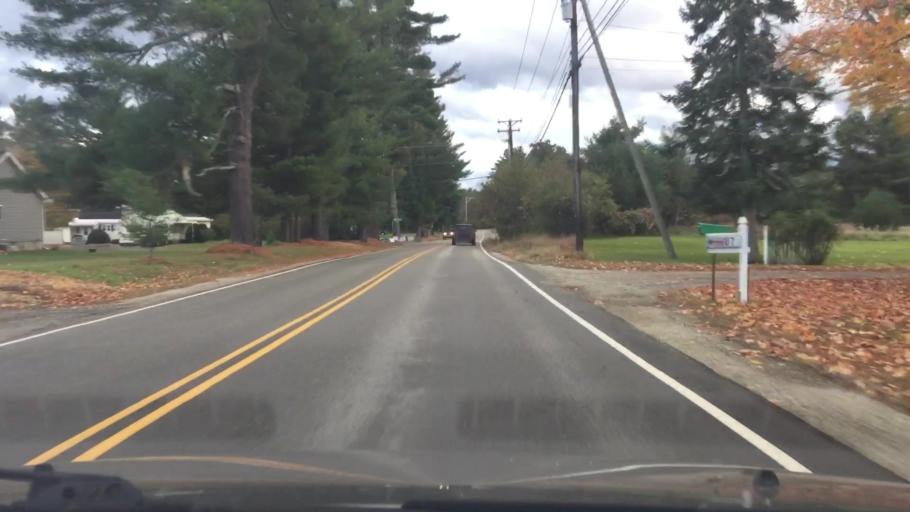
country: US
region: New Hampshire
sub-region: Cheshire County
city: Swanzey
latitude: 42.8554
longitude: -72.2785
